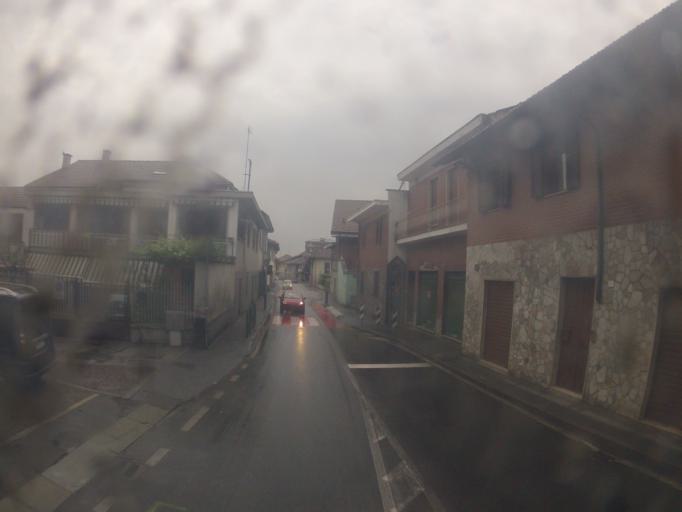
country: IT
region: Piedmont
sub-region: Provincia di Torino
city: La Loggia
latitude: 44.9548
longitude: 7.6683
